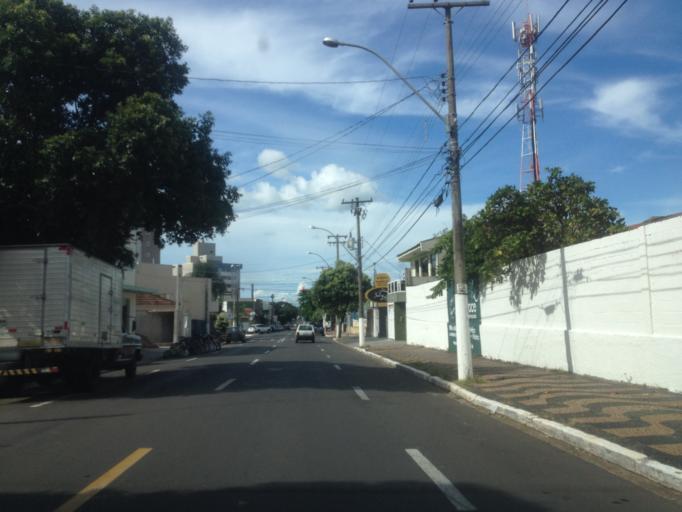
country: BR
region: Sao Paulo
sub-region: Marilia
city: Marilia
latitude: -22.2186
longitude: -49.9399
